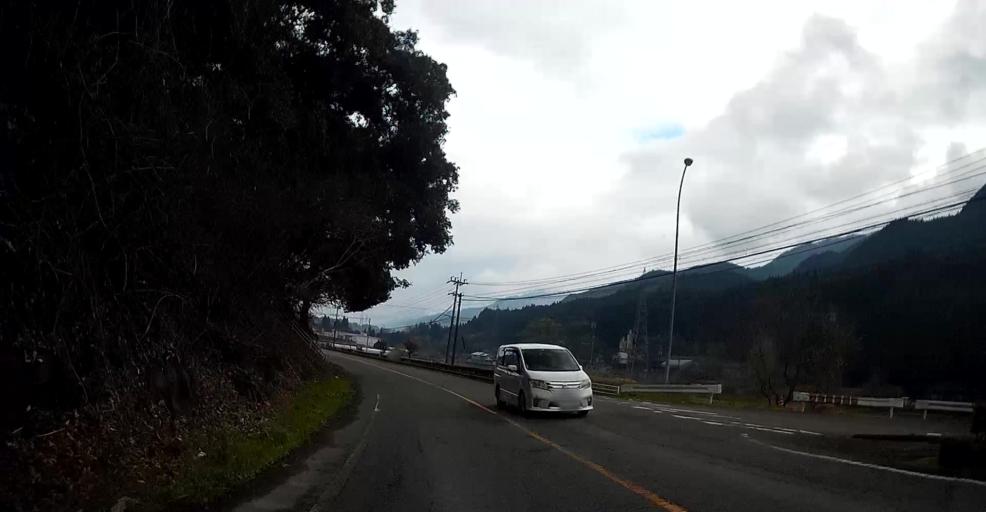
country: JP
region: Kumamoto
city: Matsubase
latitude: 32.6140
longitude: 130.8460
